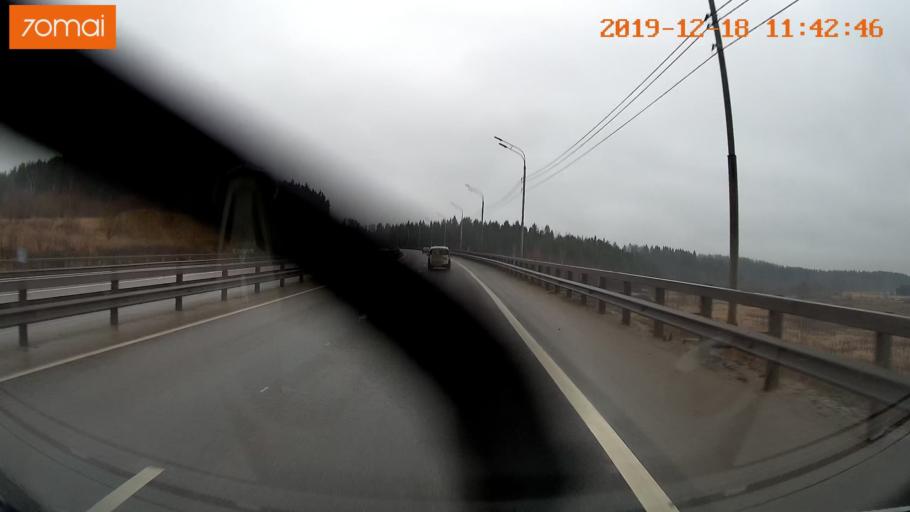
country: RU
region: Moskovskaya
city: Zvenigorod
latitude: 55.7273
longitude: 36.8798
